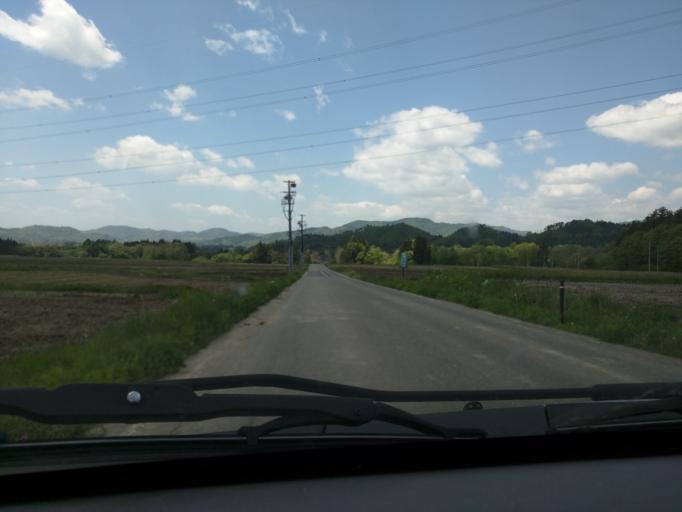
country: JP
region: Fukushima
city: Kitakata
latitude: 37.6402
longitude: 139.7967
